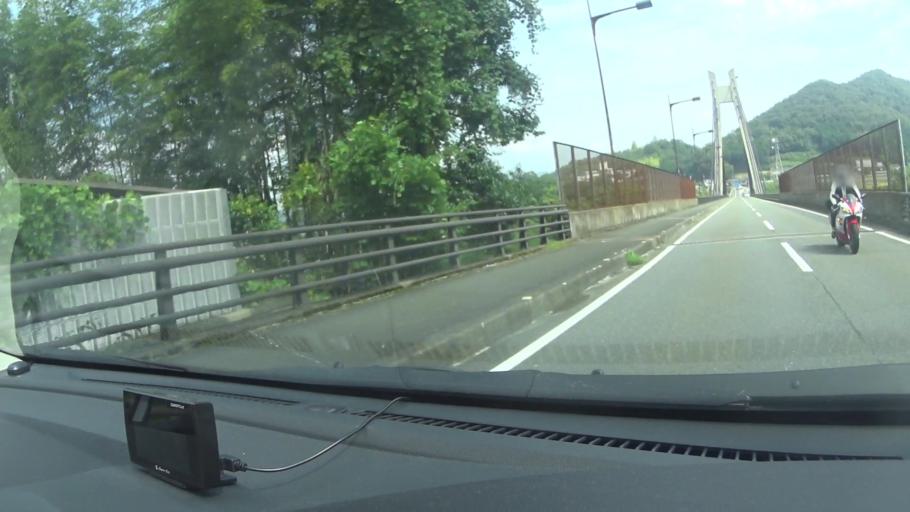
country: JP
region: Kyoto
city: Ayabe
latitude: 35.2899
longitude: 135.2657
